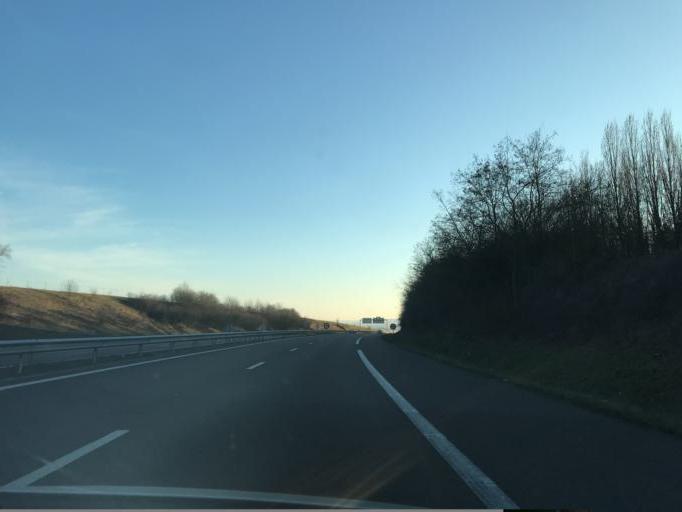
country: FR
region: Bourgogne
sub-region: Departement de l'Yonne
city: Soucy
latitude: 48.2672
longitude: 3.2925
